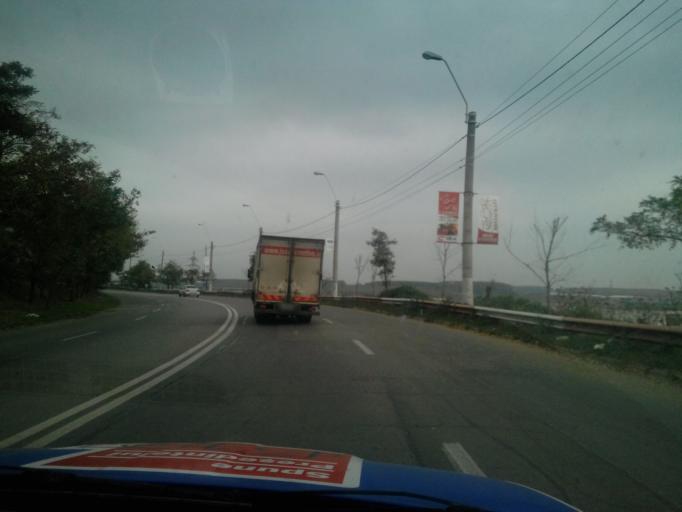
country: RO
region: Braila
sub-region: Municipiul Braila
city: Braila
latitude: 45.2867
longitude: 27.9789
